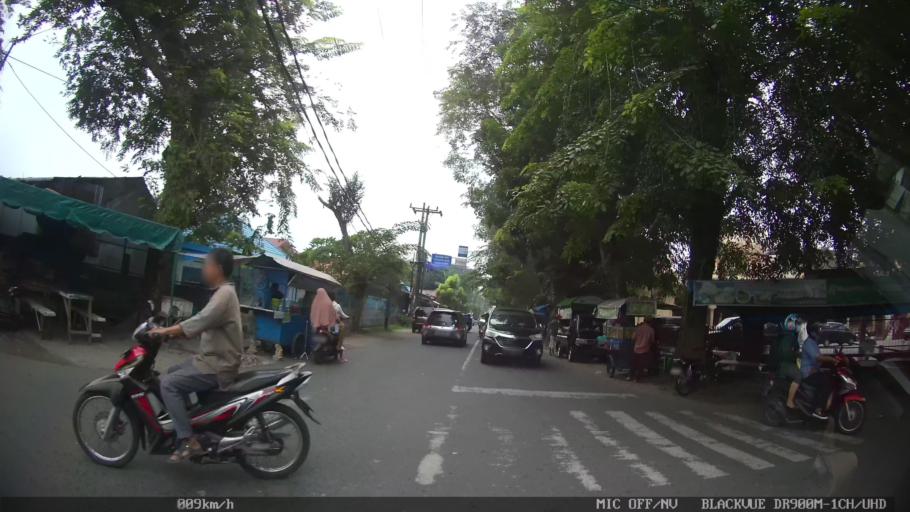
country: ID
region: North Sumatra
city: Medan
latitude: 3.5632
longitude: 98.6944
